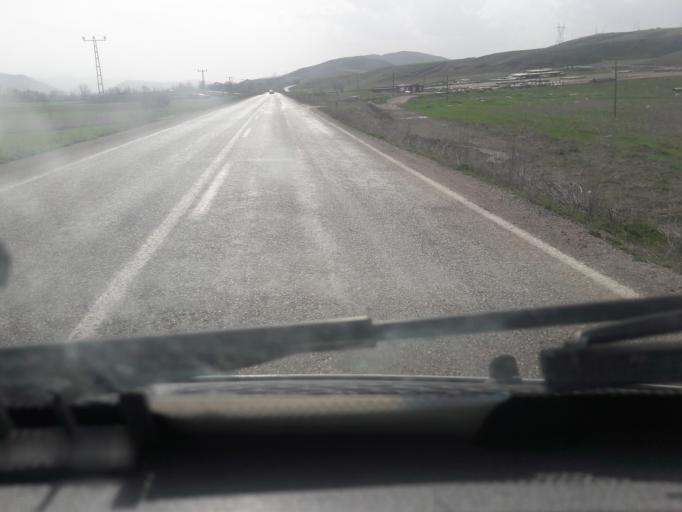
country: TR
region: Gumushane
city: Kelkit
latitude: 40.1431
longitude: 39.4071
